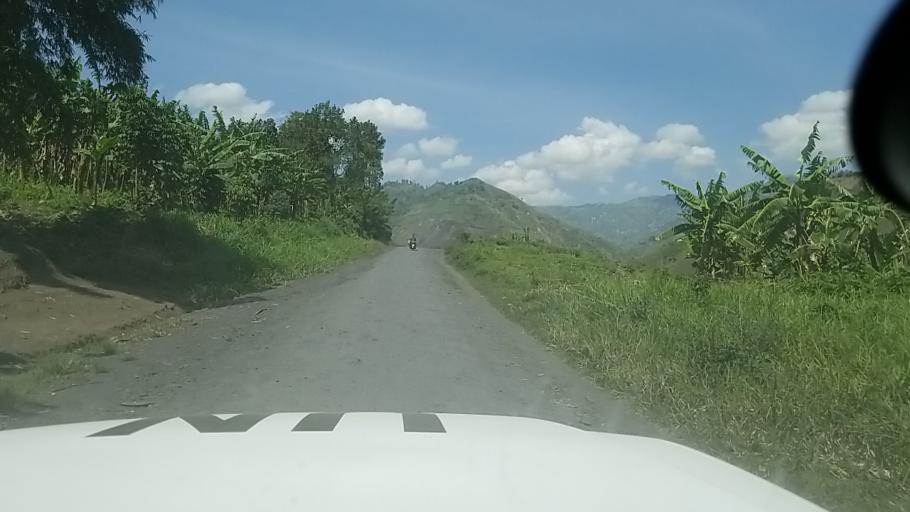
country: CD
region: Nord Kivu
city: Sake
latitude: -1.7397
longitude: 28.9997
